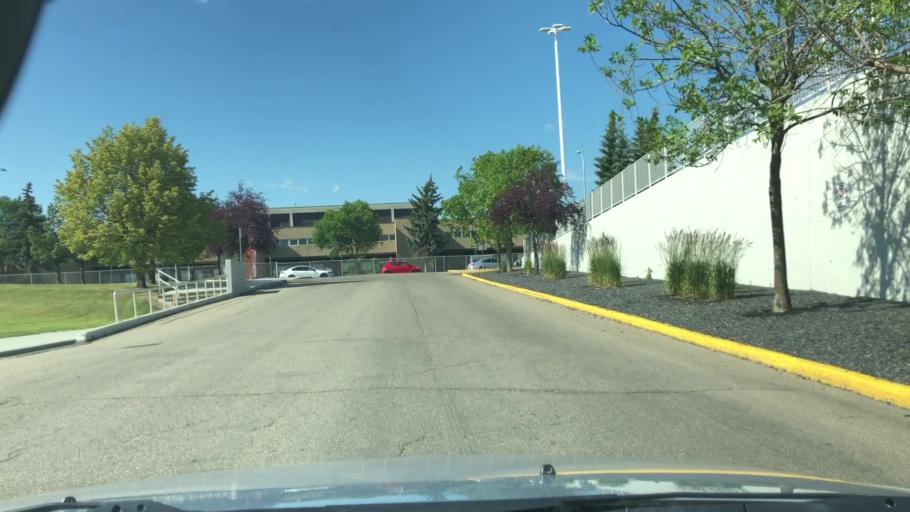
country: CA
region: Alberta
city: Edmonton
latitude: 53.6041
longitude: -113.4443
